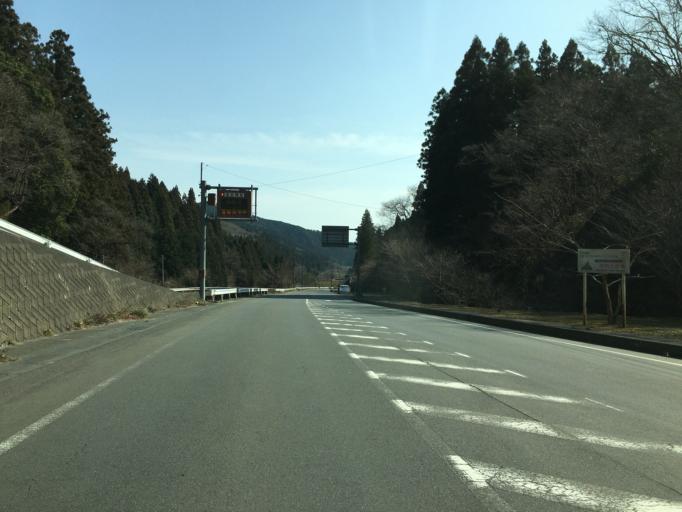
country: JP
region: Ibaraki
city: Daigo
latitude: 36.7949
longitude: 140.4755
